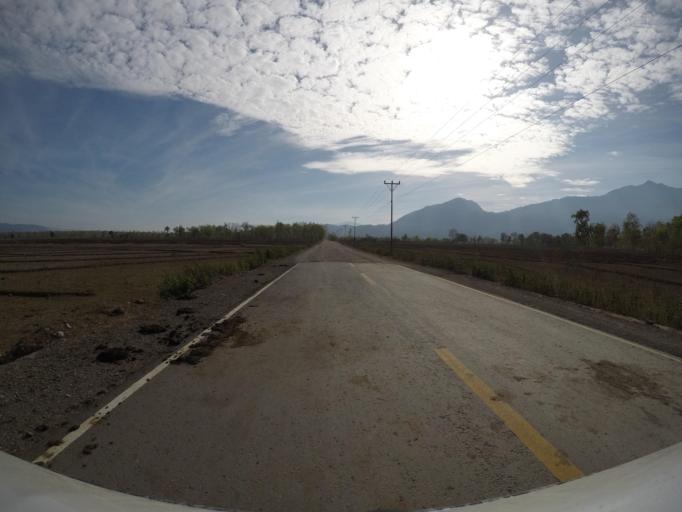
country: TL
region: Bobonaro
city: Maliana
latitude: -8.9324
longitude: 125.1982
